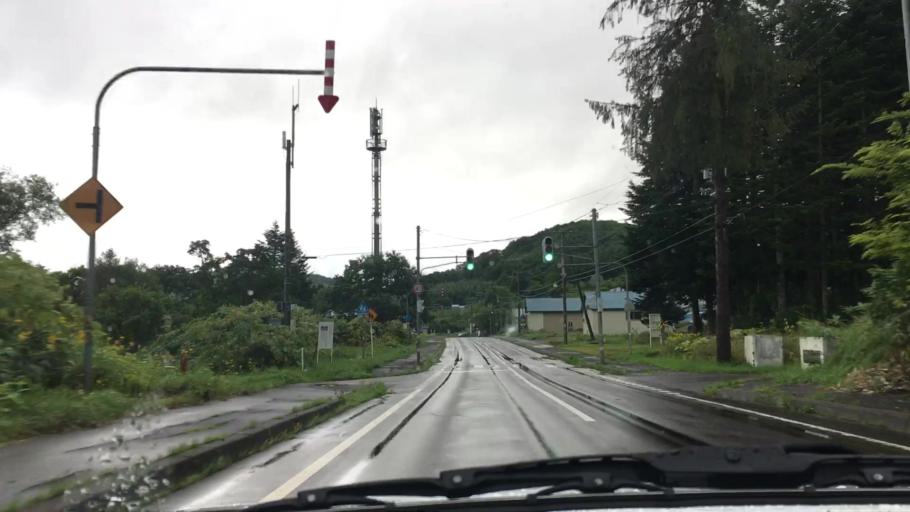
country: JP
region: Hokkaido
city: Niseko Town
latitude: 42.6477
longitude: 140.7342
